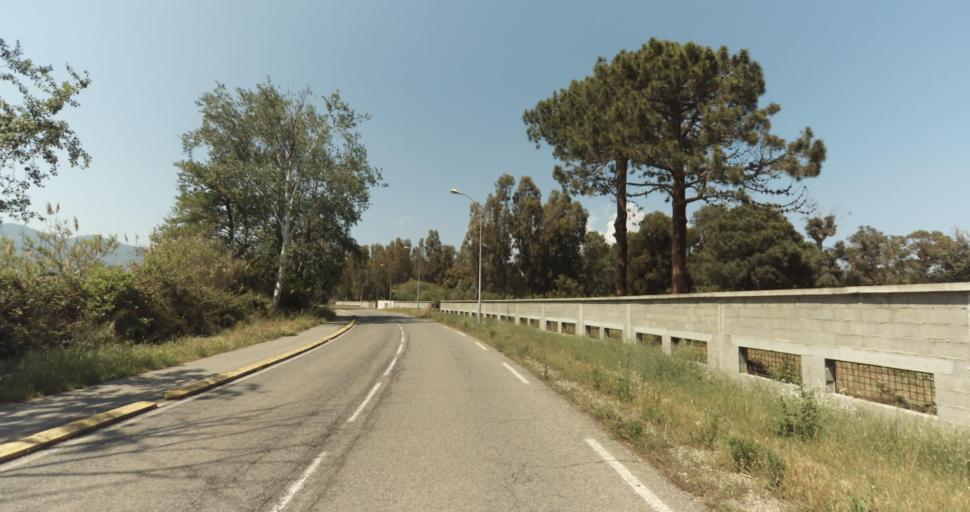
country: FR
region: Corsica
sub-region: Departement de la Haute-Corse
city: Biguglia
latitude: 42.6219
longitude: 9.4736
